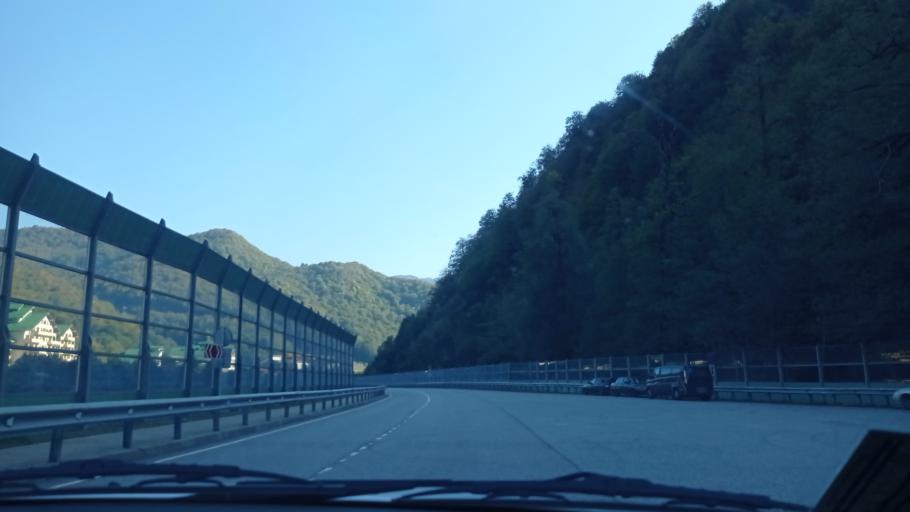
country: RU
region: Krasnodarskiy
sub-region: Sochi City
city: Krasnaya Polyana
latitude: 43.6918
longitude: 40.2710
